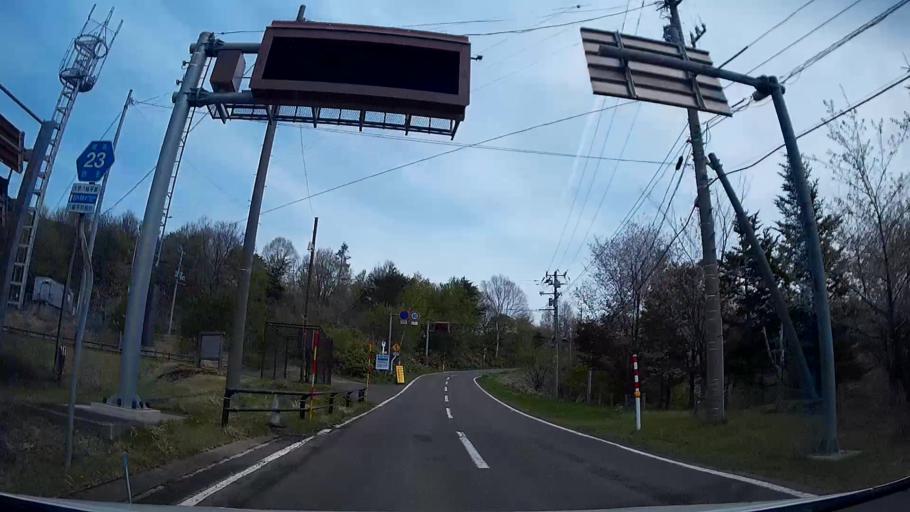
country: JP
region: Iwate
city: Shizukuishi
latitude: 39.9219
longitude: 140.9758
